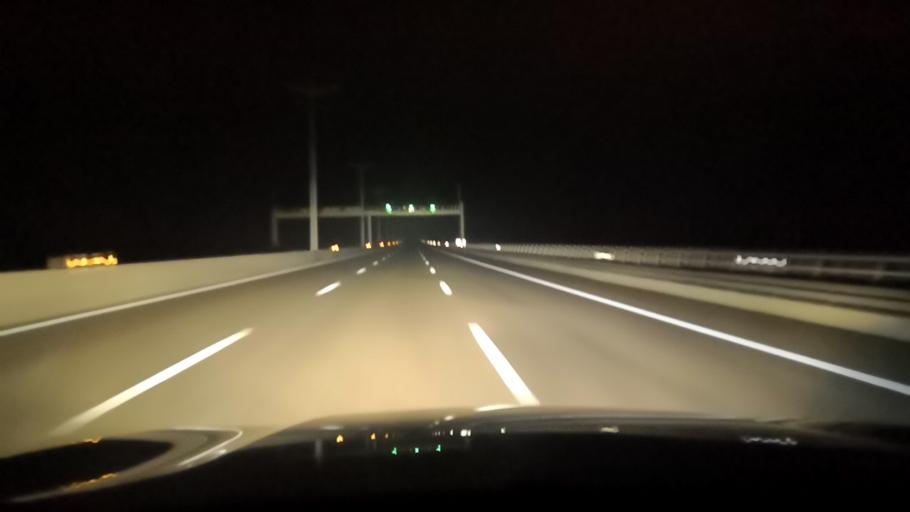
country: PT
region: Santarem
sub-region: Benavente
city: Samora Correia
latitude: 38.9831
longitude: -8.8872
